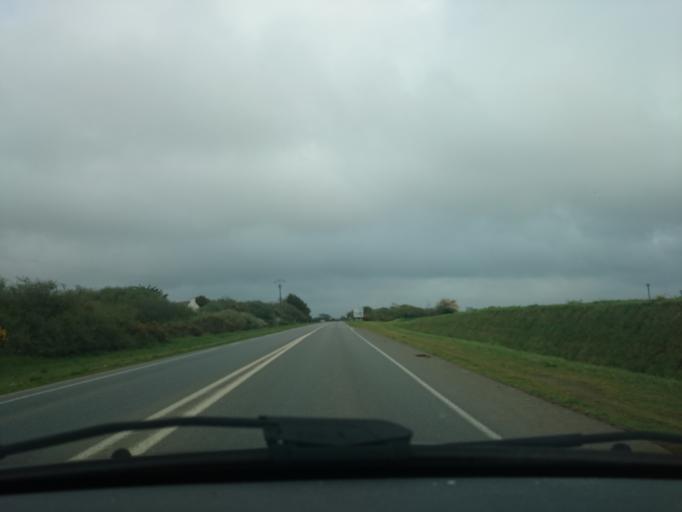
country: FR
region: Brittany
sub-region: Departement du Finistere
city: Lanrivoare
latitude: 48.4701
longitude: -4.6449
